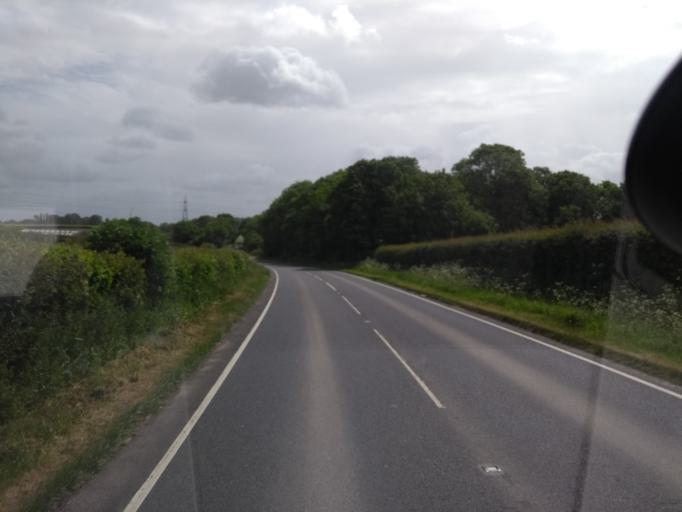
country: GB
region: England
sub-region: Somerset
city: Bridgwater
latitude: 51.1775
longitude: -3.1050
